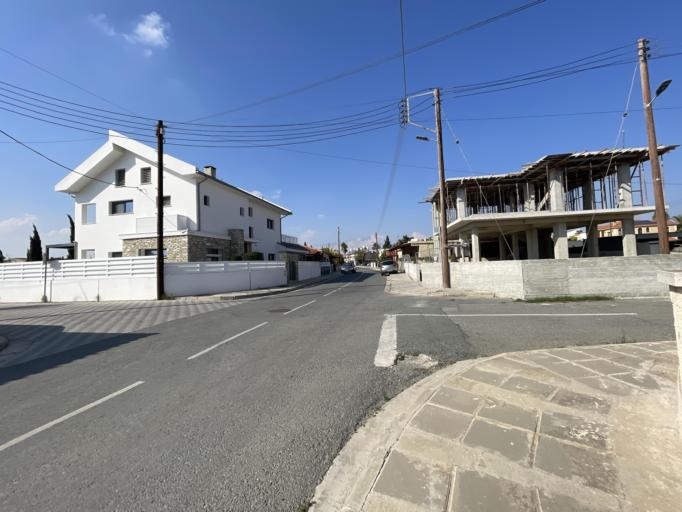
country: CY
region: Larnaka
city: Kiti
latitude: 34.8454
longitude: 33.5745
